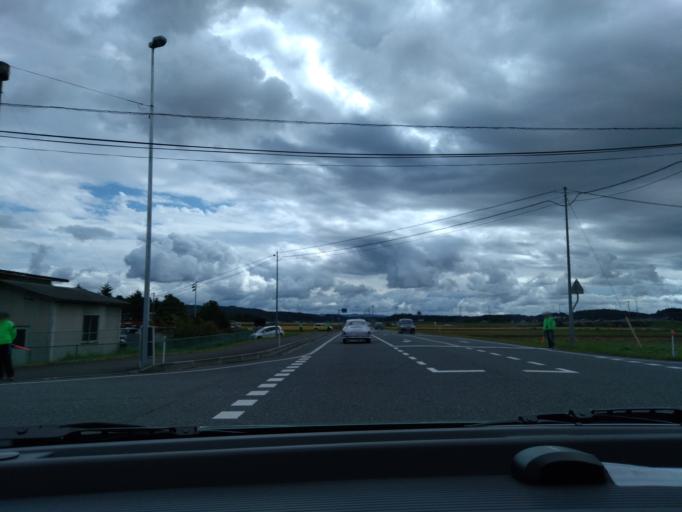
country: JP
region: Iwate
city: Ichinoseki
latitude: 38.8332
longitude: 141.1901
